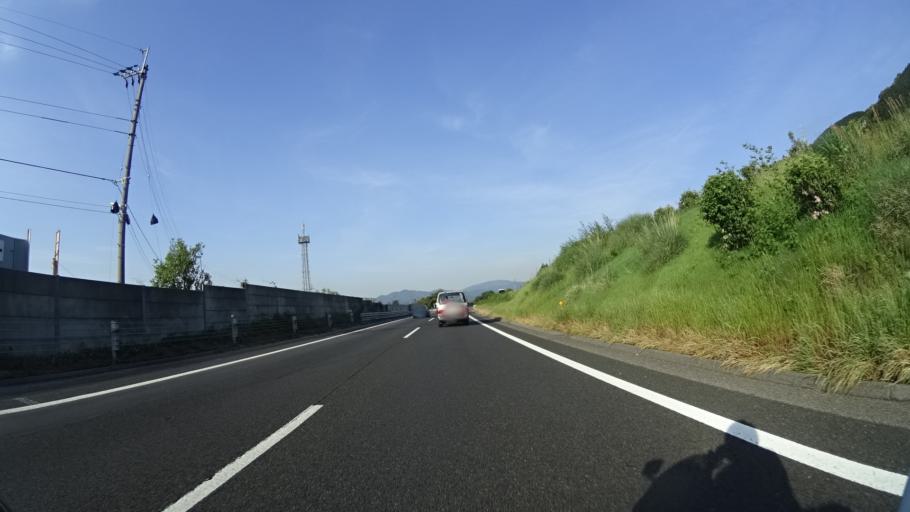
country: JP
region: Ehime
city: Kawanoecho
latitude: 33.9675
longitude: 133.5432
